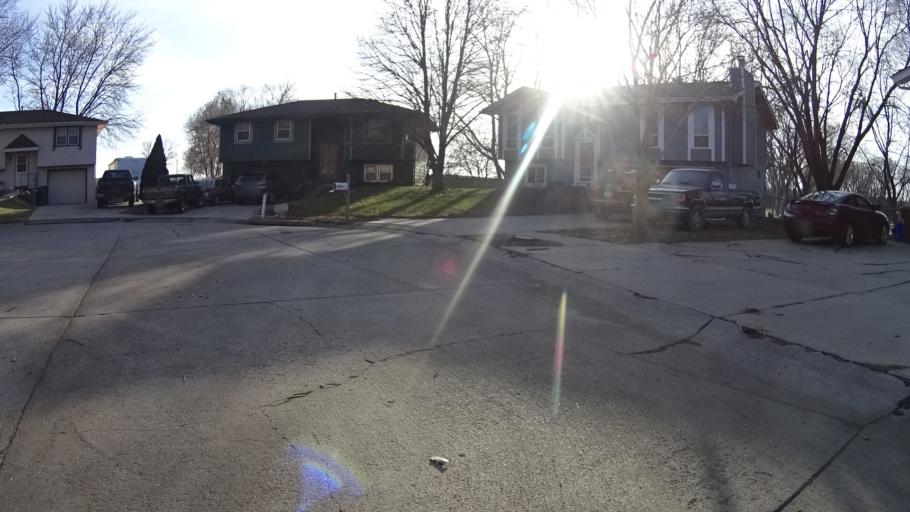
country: US
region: Nebraska
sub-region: Sarpy County
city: La Vista
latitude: 41.1853
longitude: -95.9979
